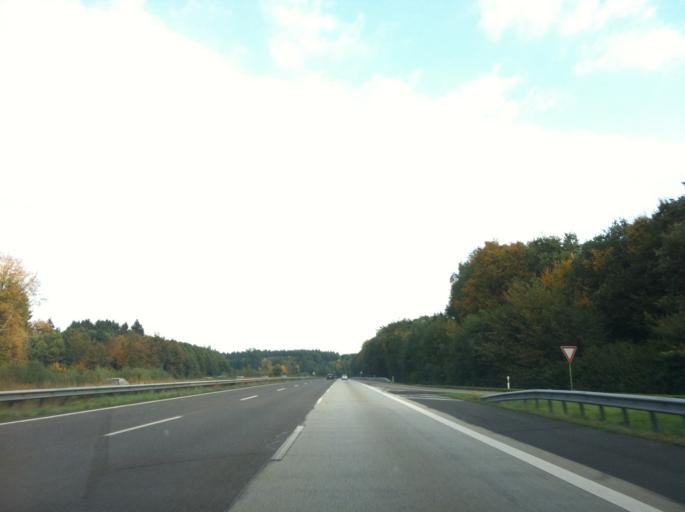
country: DE
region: Rheinland-Pfalz
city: Stebach
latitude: 50.5232
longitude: 7.6633
